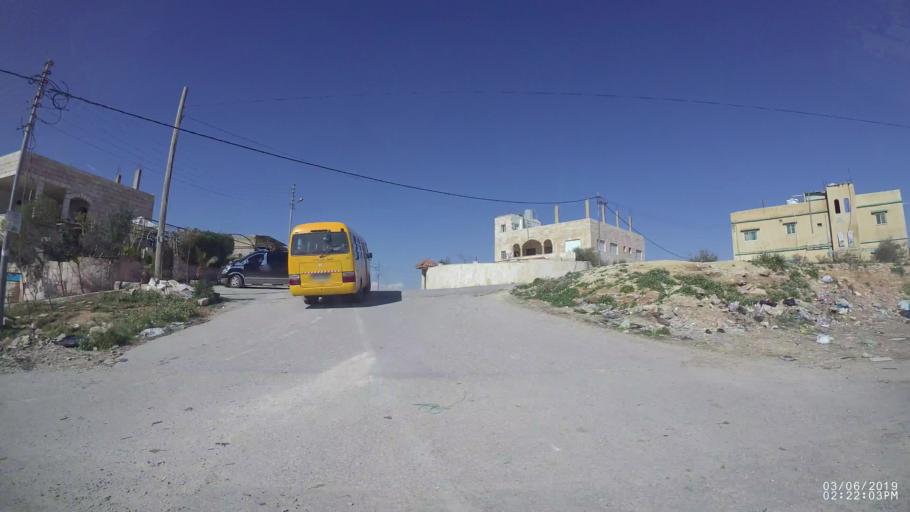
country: JO
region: Zarqa
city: Russeifa
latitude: 32.0419
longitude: 36.0510
